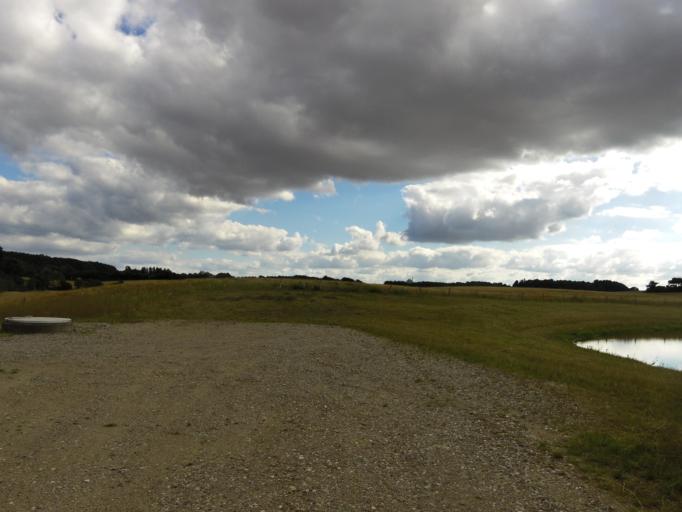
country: DK
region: South Denmark
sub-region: Haderslev Kommune
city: Haderslev
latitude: 55.2336
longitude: 9.4843
